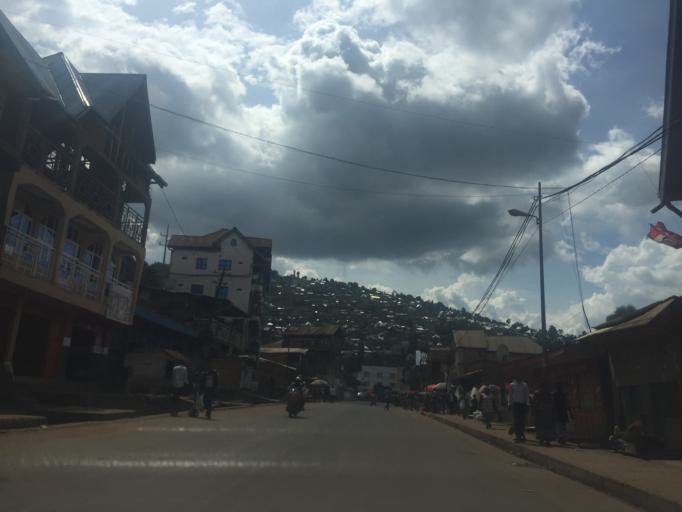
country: CD
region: South Kivu
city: Bukavu
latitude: -2.4830
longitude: 28.8411
